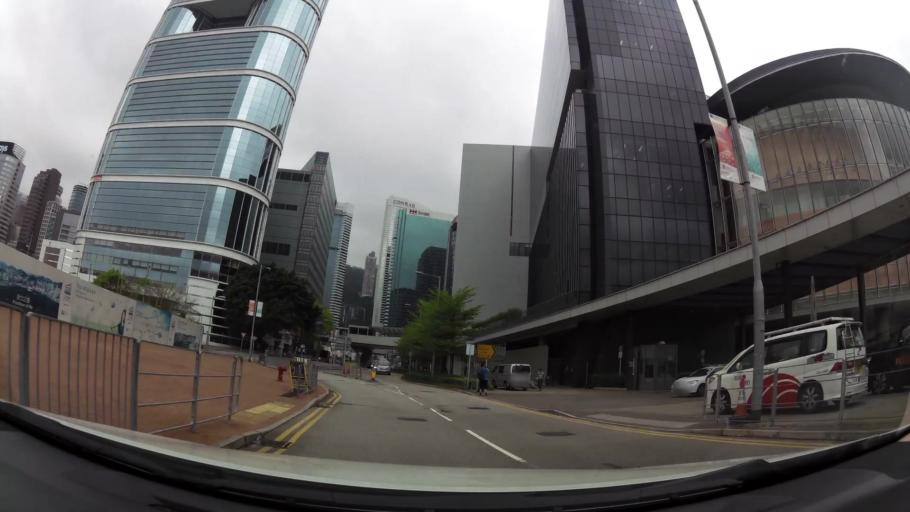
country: HK
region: Wanchai
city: Wan Chai
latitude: 22.2817
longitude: 114.1669
